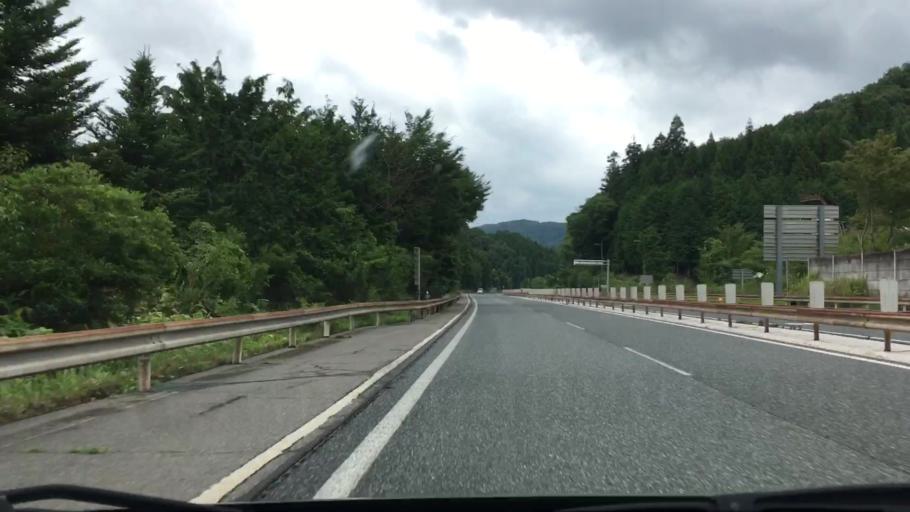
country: JP
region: Okayama
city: Niimi
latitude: 35.0016
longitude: 133.4726
